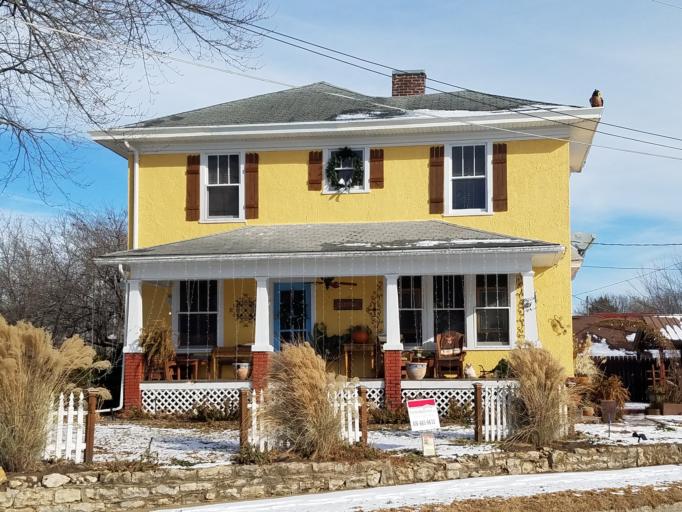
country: US
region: Missouri
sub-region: Lafayette County
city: Lexington
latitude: 39.1858
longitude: -93.8858
